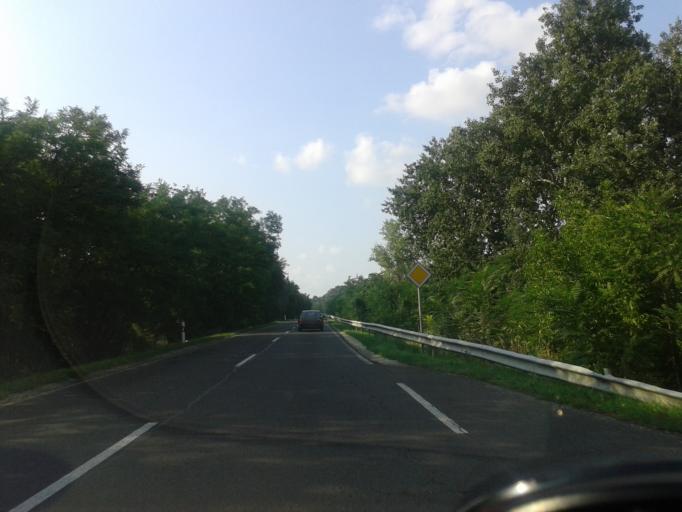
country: HU
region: Pest
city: Domsod
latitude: 47.1209
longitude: 19.0051
